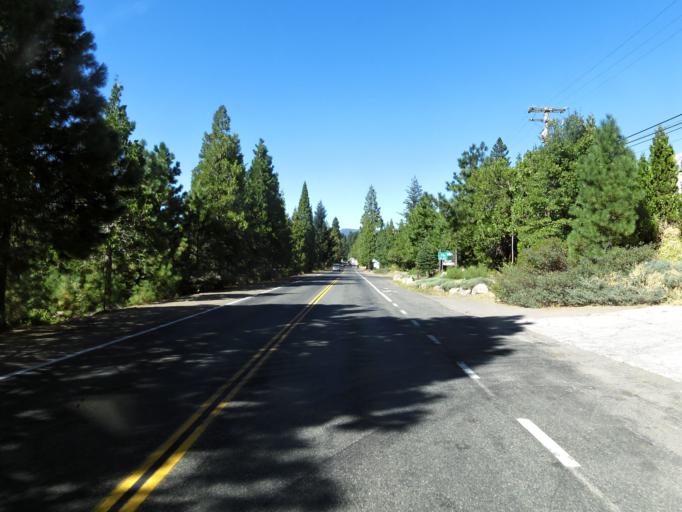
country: US
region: California
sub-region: Siskiyou County
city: Mount Shasta
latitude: 41.2976
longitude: -122.3062
